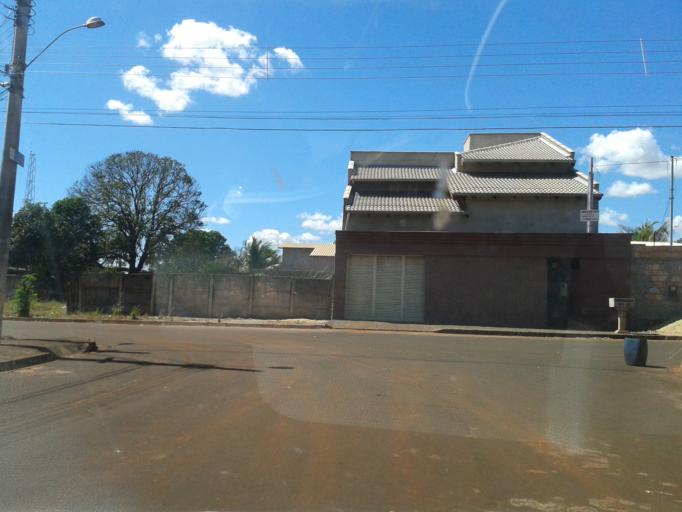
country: BR
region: Minas Gerais
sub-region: Centralina
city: Centralina
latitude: -18.5937
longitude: -49.1984
